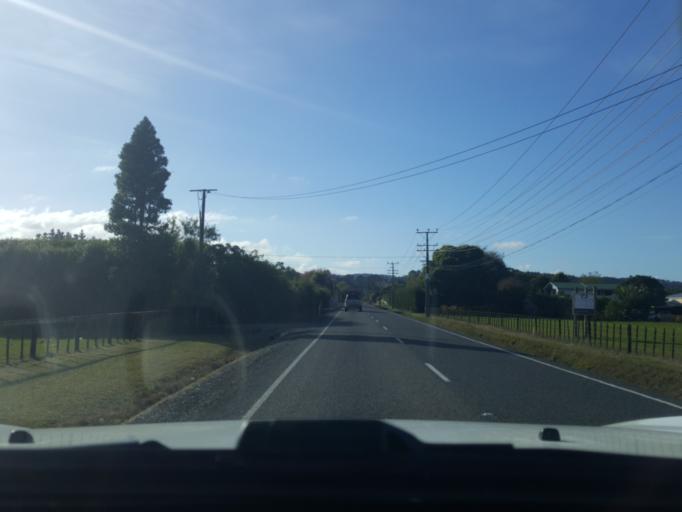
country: NZ
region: Auckland
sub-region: Auckland
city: Muriwai Beach
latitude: -36.7684
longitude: 174.5762
